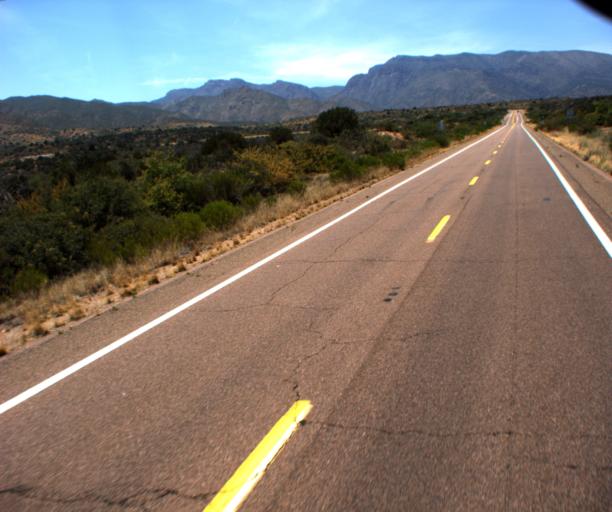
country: US
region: Arizona
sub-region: Gila County
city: Payson
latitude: 34.0325
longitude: -111.3578
